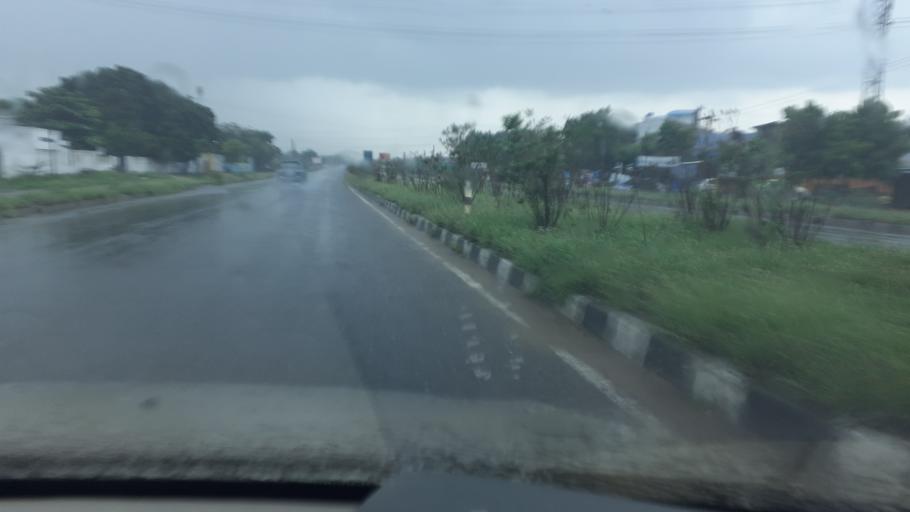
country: IN
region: Tamil Nadu
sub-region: Virudhunagar
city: Virudunagar
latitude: 9.5965
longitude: 77.9480
